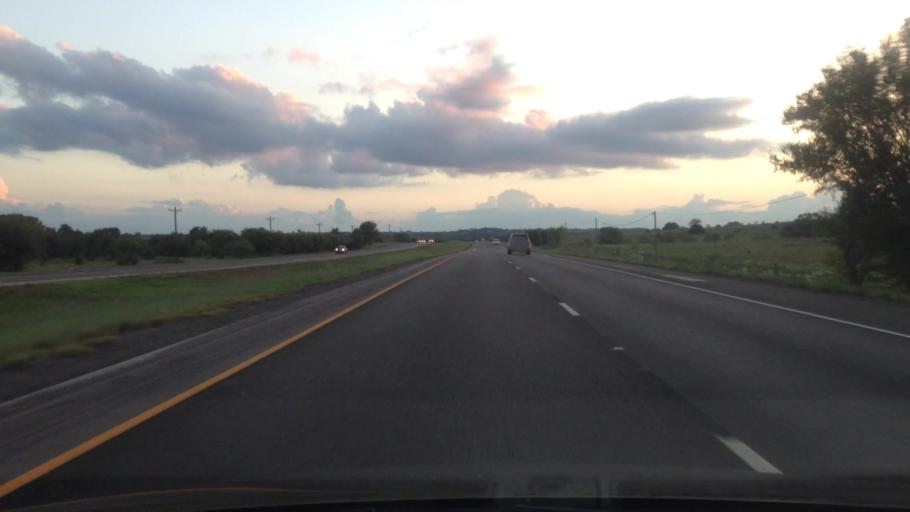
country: US
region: Texas
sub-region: Parker County
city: Aledo
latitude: 32.5931
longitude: -97.5838
